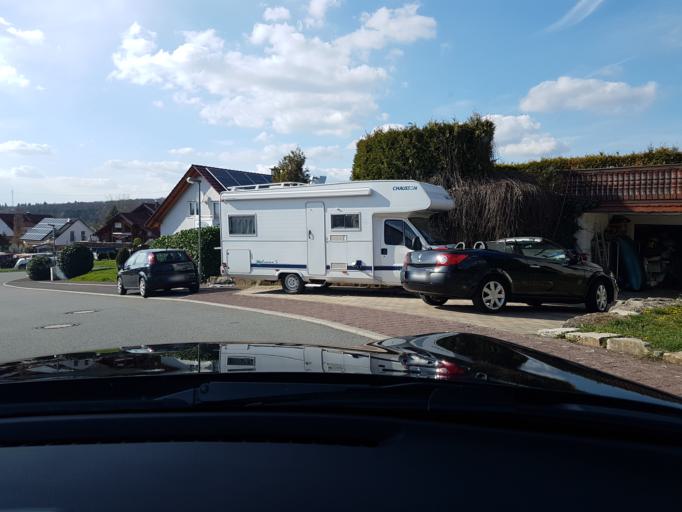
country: DE
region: Baden-Wuerttemberg
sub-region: Karlsruhe Region
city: Osterburken
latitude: 49.4220
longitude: 9.4227
